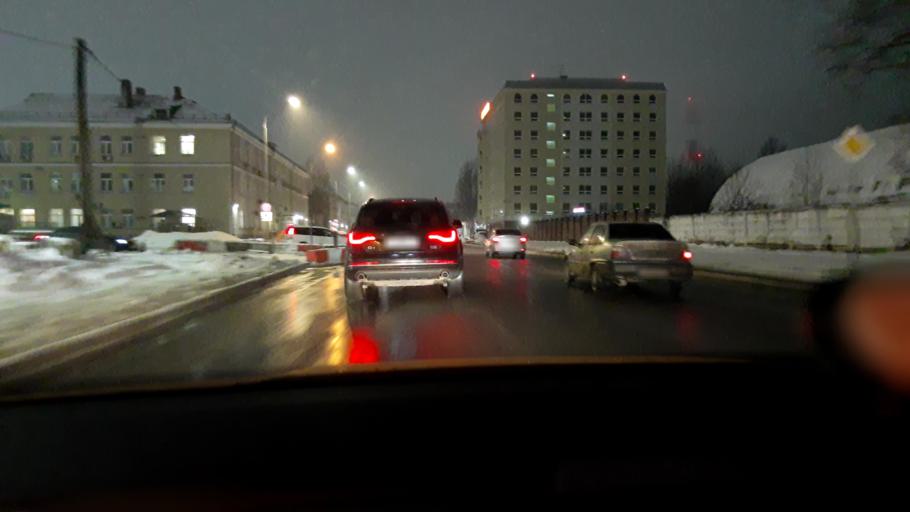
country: RU
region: Moskovskaya
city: Lobnya
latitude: 55.9835
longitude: 37.4116
